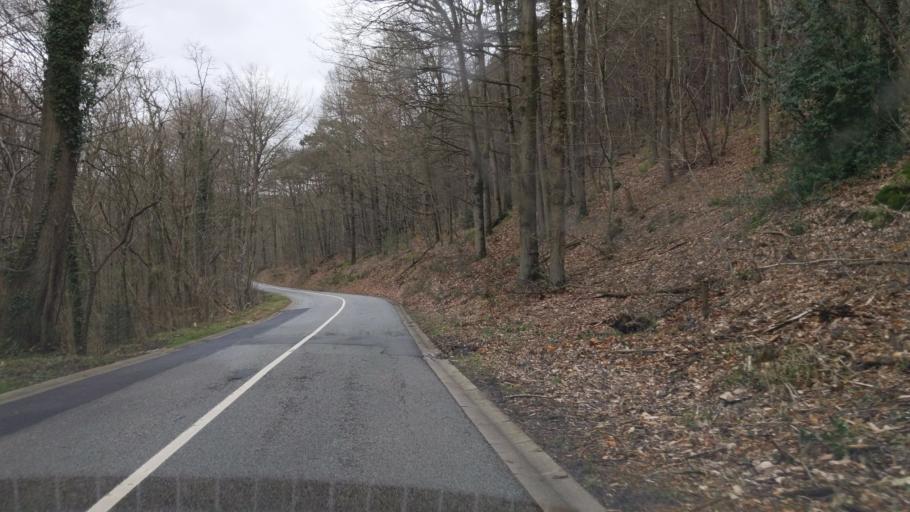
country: FR
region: Ile-de-France
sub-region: Departement des Yvelines
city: Chevreuse
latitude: 48.6844
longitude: 2.0263
